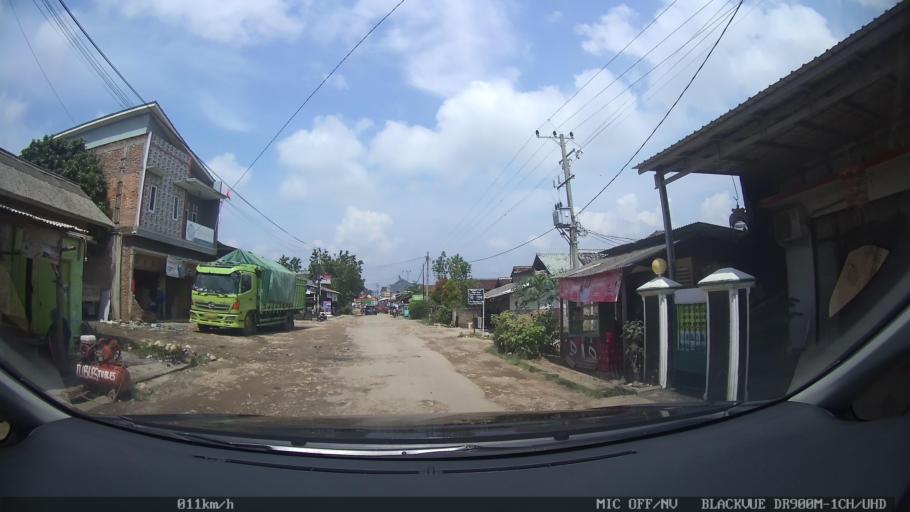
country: ID
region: Lampung
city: Kedaton
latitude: -5.3378
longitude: 105.2954
